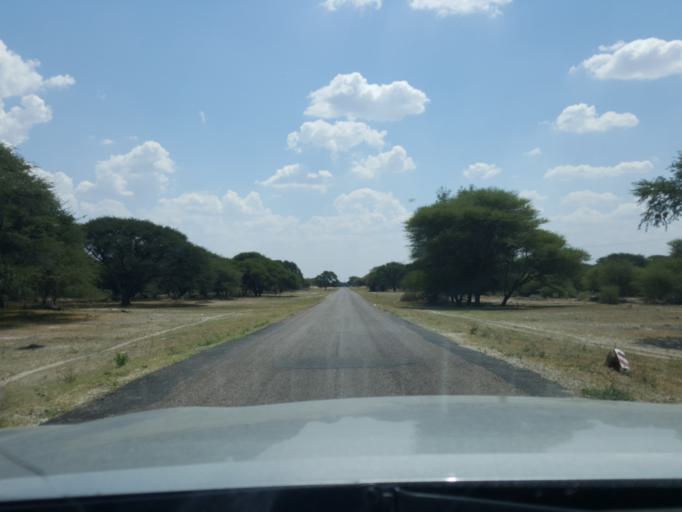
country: BW
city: Tsau
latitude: -20.1838
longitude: 22.4690
